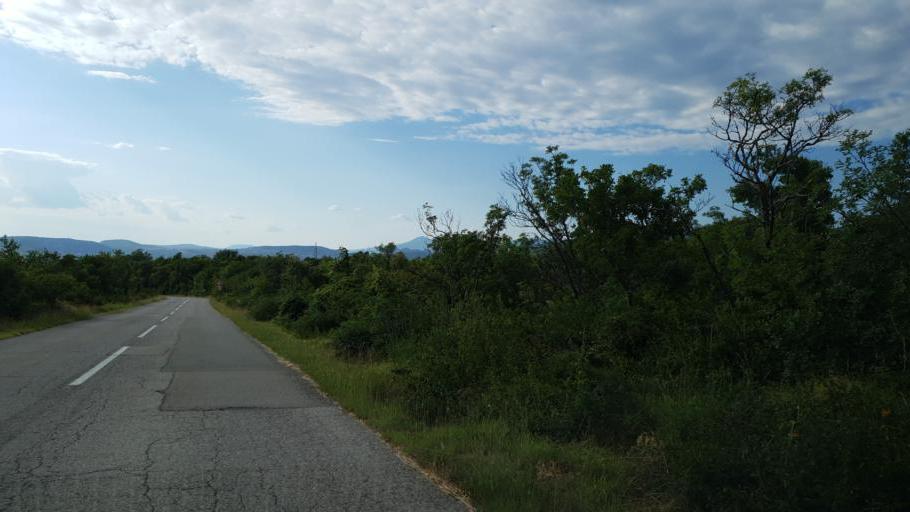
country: HR
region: Primorsko-Goranska
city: Hreljin
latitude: 45.2700
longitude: 14.5869
